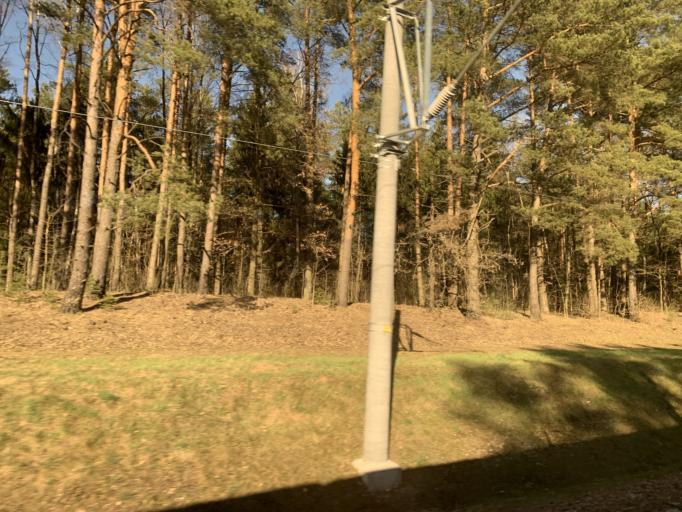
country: BY
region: Grodnenskaya
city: Astravyets
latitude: 54.5773
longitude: 25.9378
